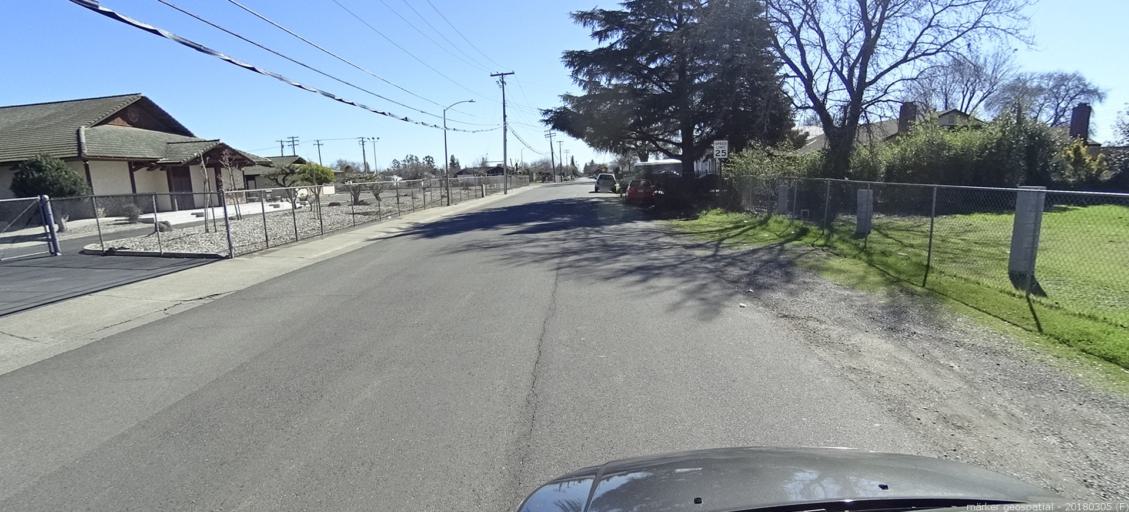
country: US
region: California
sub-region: Sacramento County
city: Florin
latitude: 38.4953
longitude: -121.3998
